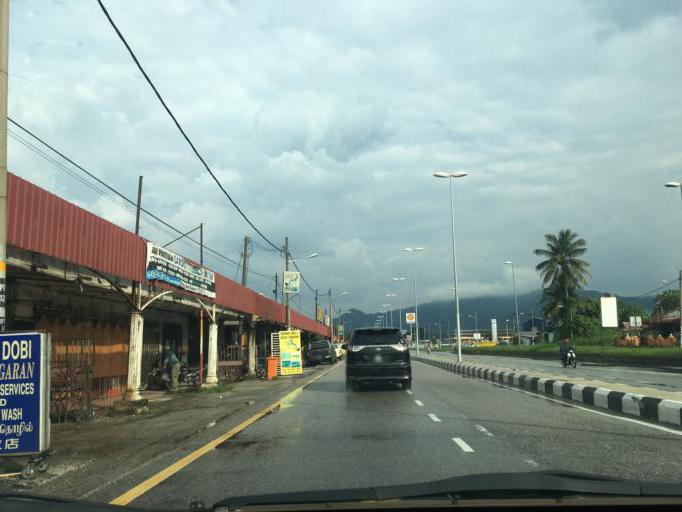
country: MY
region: Selangor
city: Rawang
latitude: 3.3142
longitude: 101.5791
